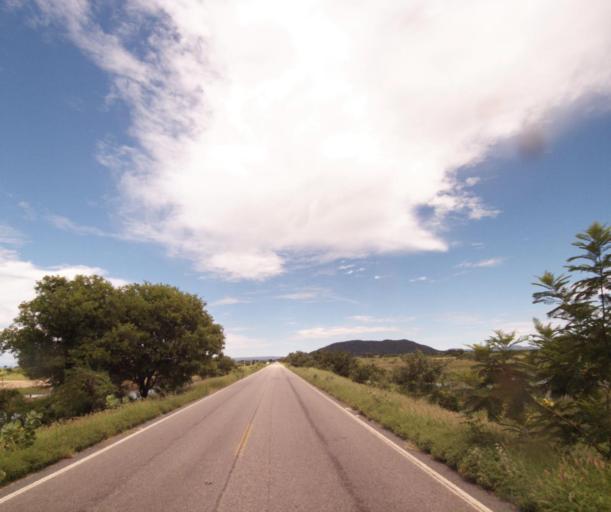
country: BR
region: Bahia
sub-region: Guanambi
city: Guanambi
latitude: -14.2282
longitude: -42.9159
